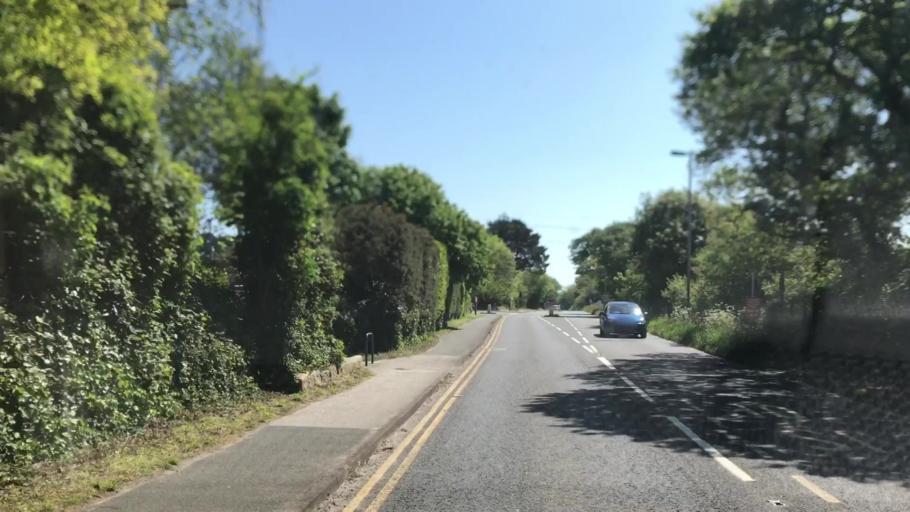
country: GB
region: England
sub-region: Cornwall
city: Chacewater
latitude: 50.2641
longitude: -5.1258
